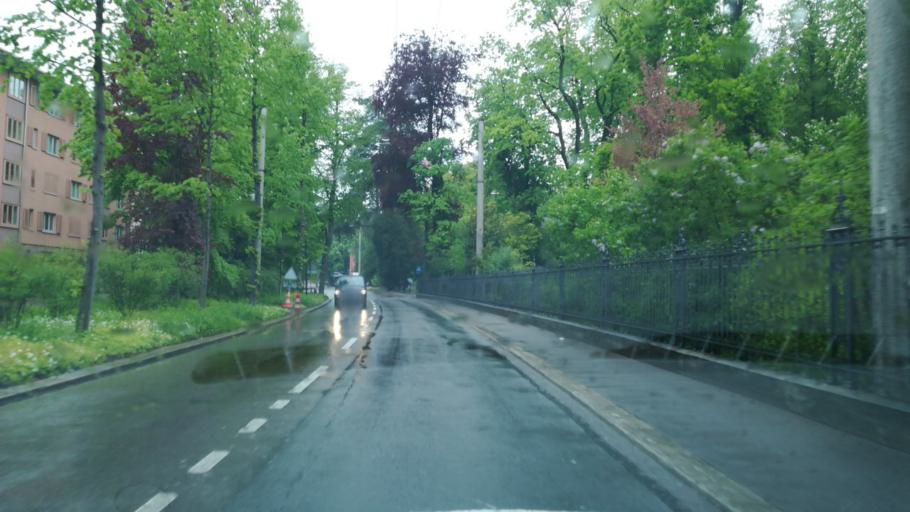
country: CH
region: Zurich
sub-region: Bezirk Winterthur
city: Stadt Winterthur (Kreis 1) / Altstadt
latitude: 47.5029
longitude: 8.7306
